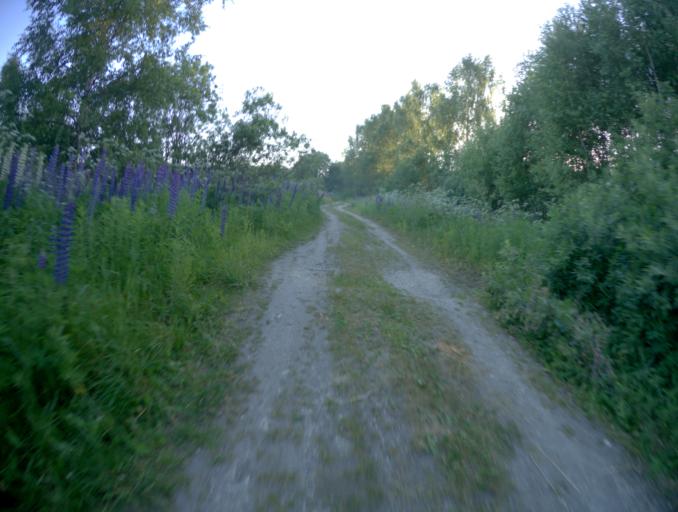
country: RU
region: Vladimir
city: Golovino
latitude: 55.9862
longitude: 40.5390
